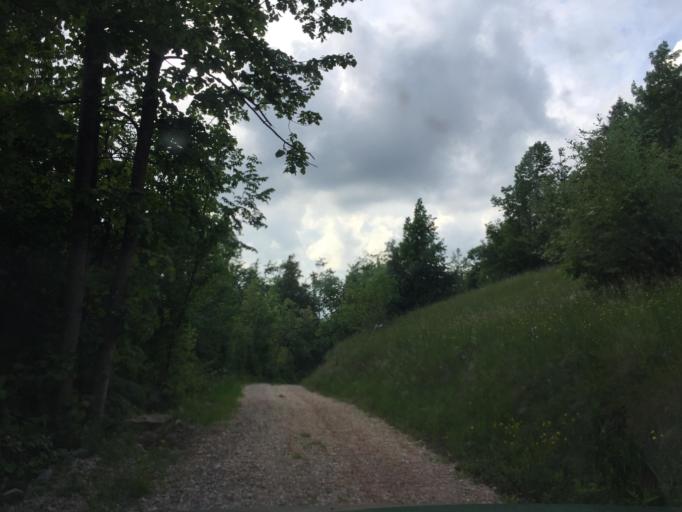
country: SI
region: Nova Gorica
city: Sempas
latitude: 46.0390
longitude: 13.7674
